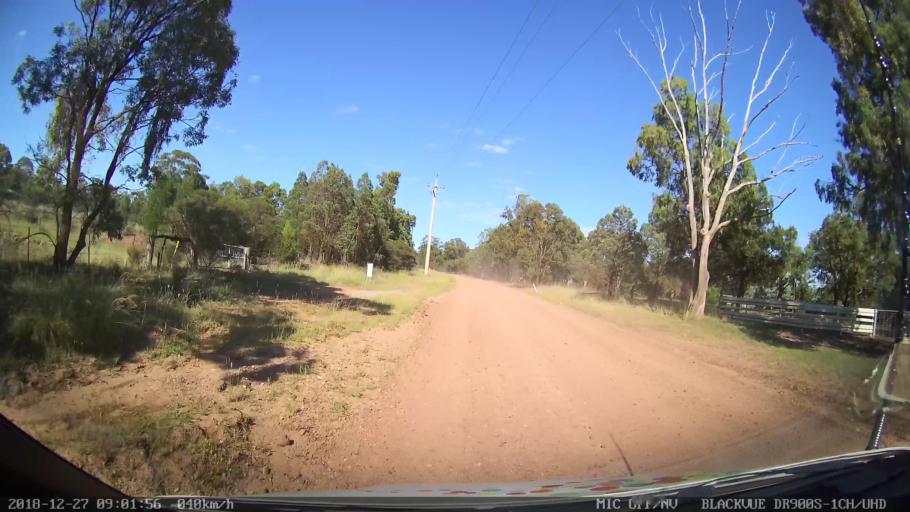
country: AU
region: New South Wales
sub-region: Lithgow
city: Portland
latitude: -33.1017
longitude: 150.2127
